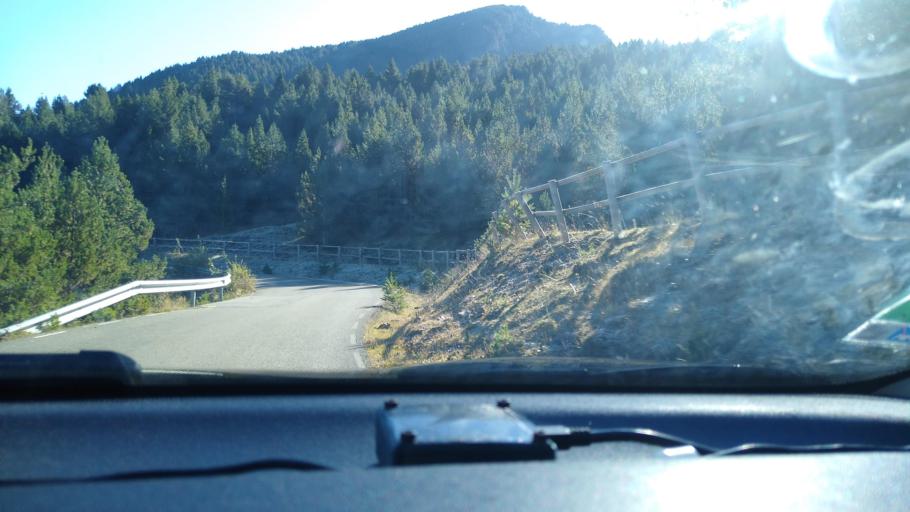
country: ES
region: Catalonia
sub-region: Provincia de Barcelona
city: Saldes
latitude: 42.1992
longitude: 1.7576
